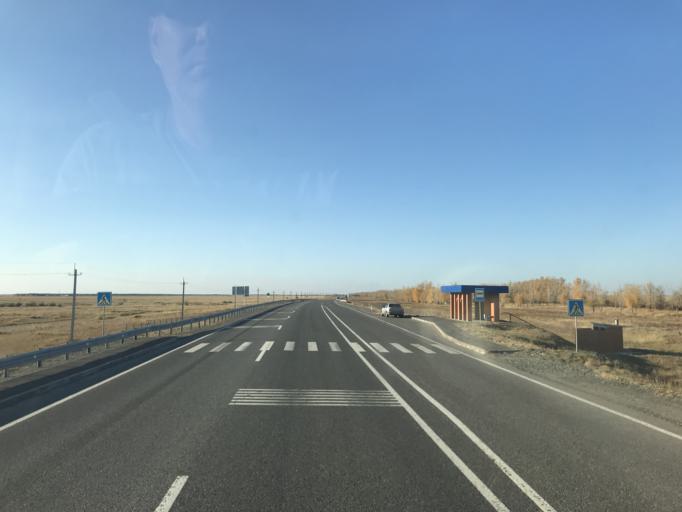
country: KZ
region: Pavlodar
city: Koktobe
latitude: 51.9280
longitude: 77.3322
